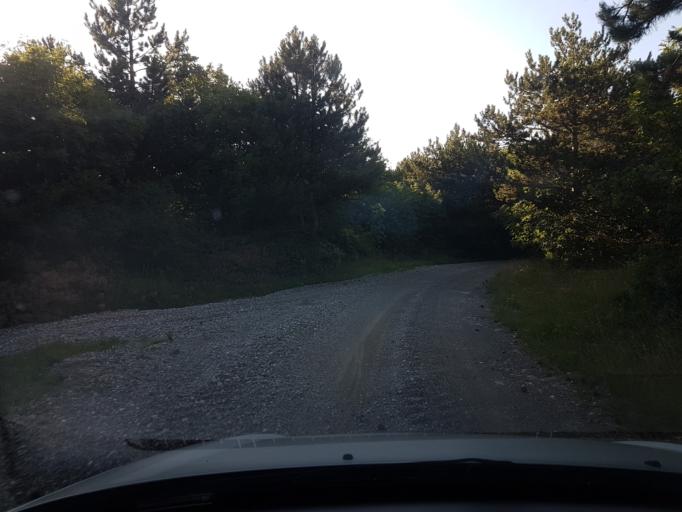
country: SI
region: Sezana
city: Sezana
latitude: 45.7163
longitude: 13.9099
